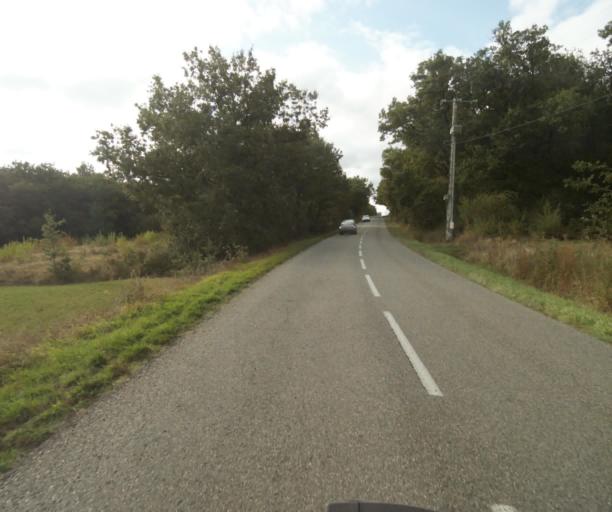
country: FR
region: Midi-Pyrenees
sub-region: Departement du Tarn-et-Garonne
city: Verdun-sur-Garonne
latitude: 43.8464
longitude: 1.1511
